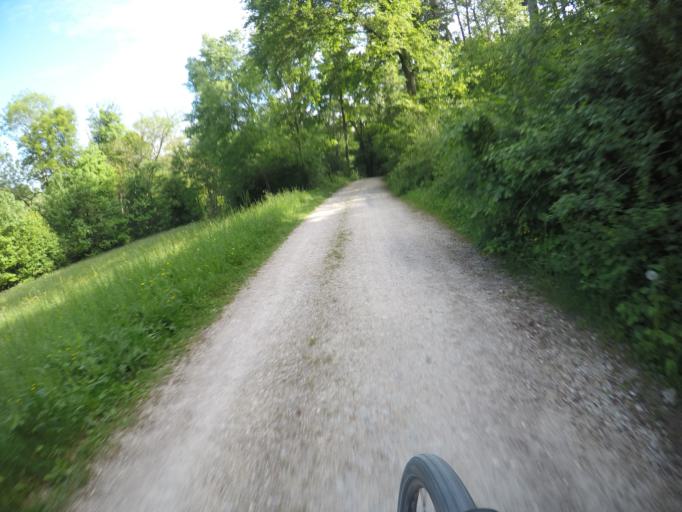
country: DE
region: Baden-Wuerttemberg
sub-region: Regierungsbezirk Stuttgart
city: Neuhausen auf den Fildern
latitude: 48.6778
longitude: 9.2975
